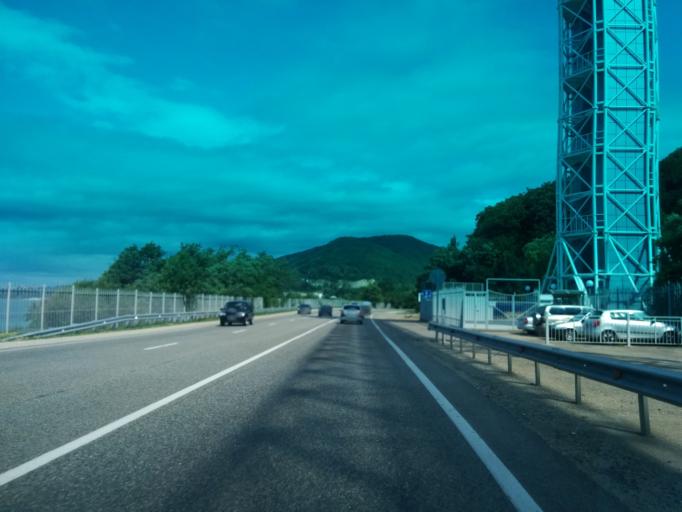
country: RU
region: Krasnodarskiy
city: Nebug
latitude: 44.1576
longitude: 39.0034
